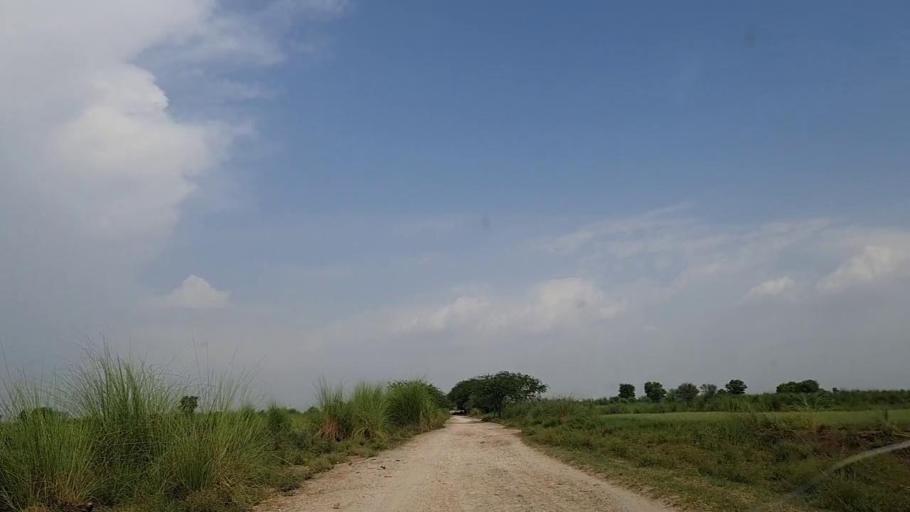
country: PK
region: Sindh
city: Khanpur
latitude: 27.8261
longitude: 69.5164
